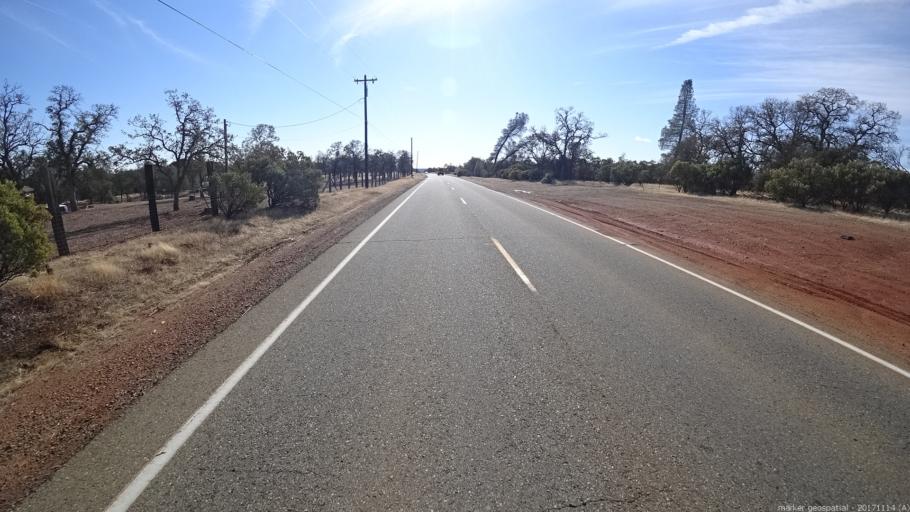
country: US
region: California
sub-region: Shasta County
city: Anderson
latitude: 40.4150
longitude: -122.4068
